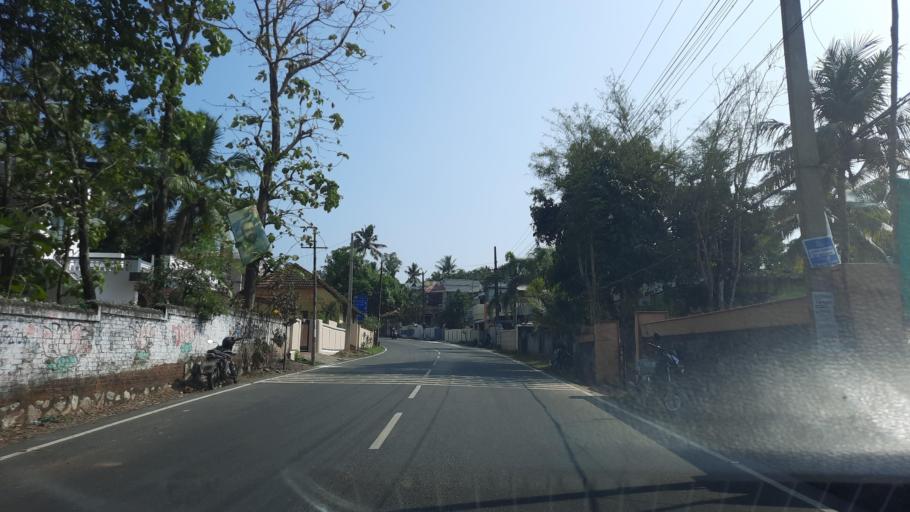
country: IN
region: Kerala
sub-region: Thiruvananthapuram
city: Thiruvananthapuram
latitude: 8.5625
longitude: 76.9209
